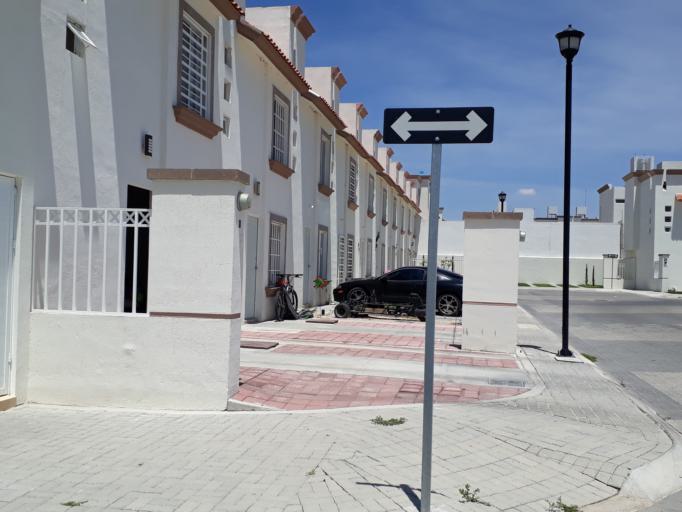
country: MX
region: Aguascalientes
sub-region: Aguascalientes
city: San Sebastian [Fraccionamiento]
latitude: 21.8105
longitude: -102.3016
